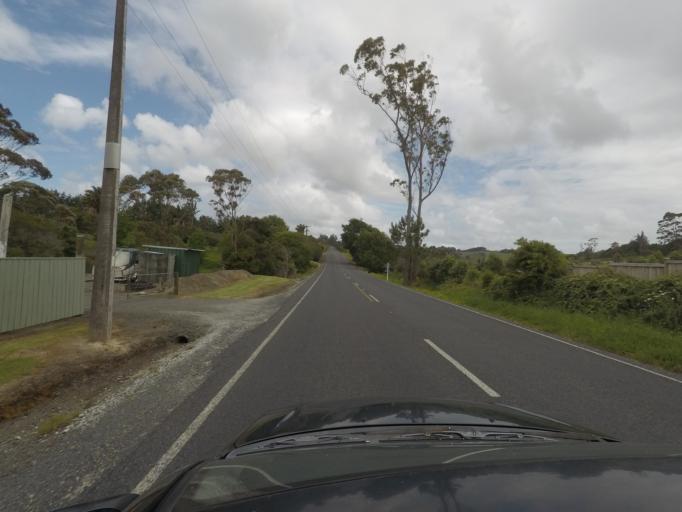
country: NZ
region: Auckland
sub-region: Auckland
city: Parakai
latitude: -36.6295
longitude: 174.5028
